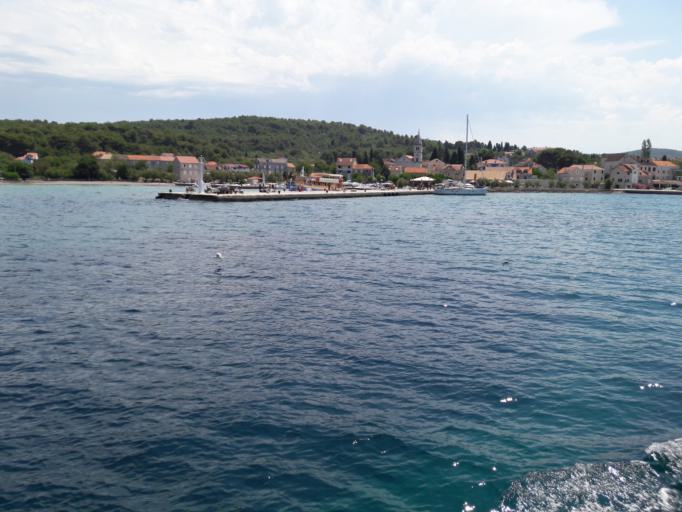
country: HR
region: Sibensko-Kniniska
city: Vodice
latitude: 43.6996
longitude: 15.8321
